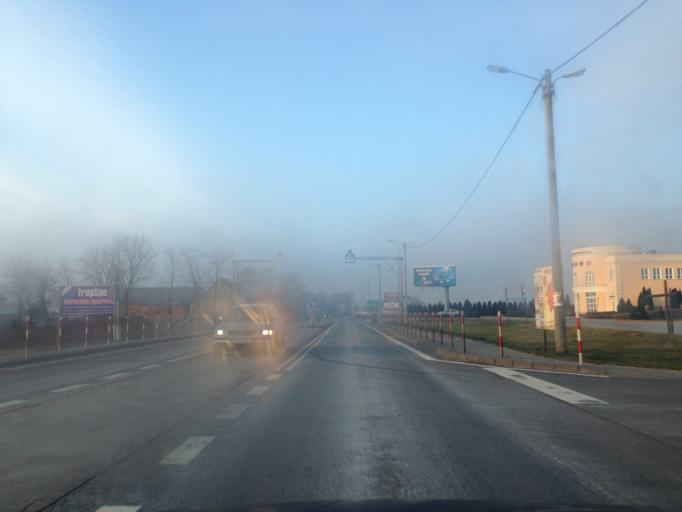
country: PL
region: Greater Poland Voivodeship
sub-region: Powiat gnieznienski
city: Lubowo
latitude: 52.5124
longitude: 17.4590
